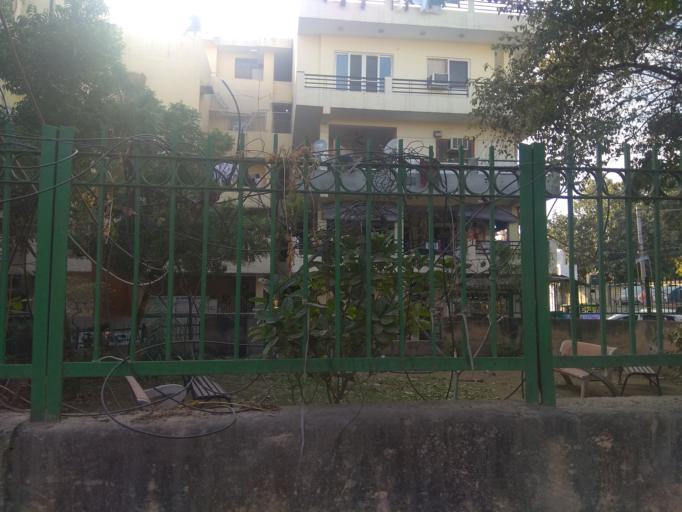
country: IN
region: NCT
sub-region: West Delhi
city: Nangloi Jat
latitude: 28.6376
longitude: 77.0678
